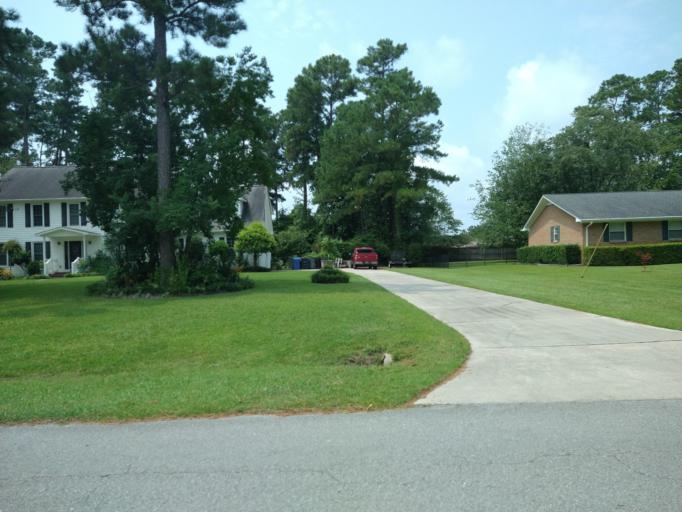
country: US
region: North Carolina
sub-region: Onslow County
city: Pumpkin Center
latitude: 34.7675
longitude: -77.3724
